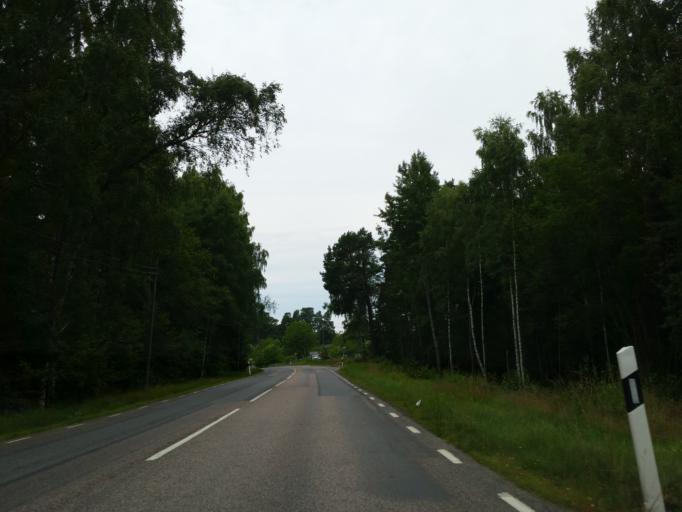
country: SE
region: Stockholm
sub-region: Sodertalje Kommun
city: Soedertaelje
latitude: 59.2015
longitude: 17.5693
